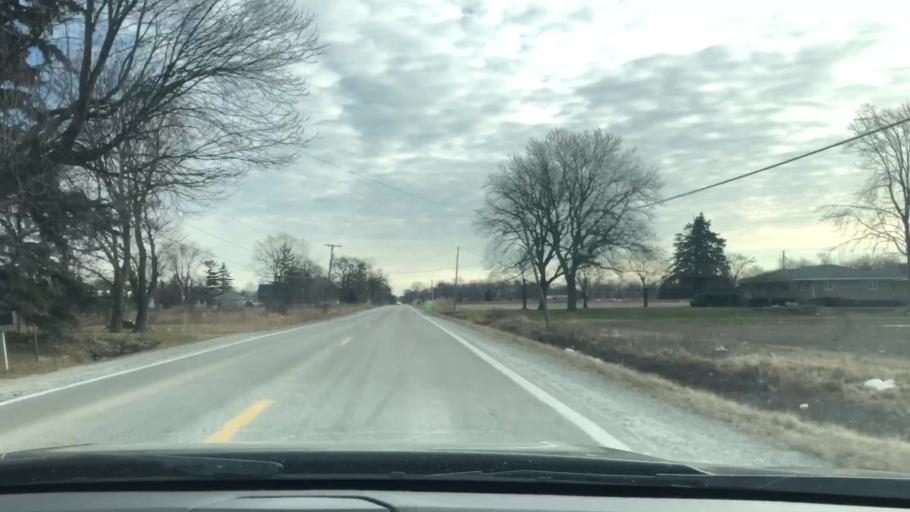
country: US
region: Michigan
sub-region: Macomb County
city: New Haven
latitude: 42.7156
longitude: -82.9136
